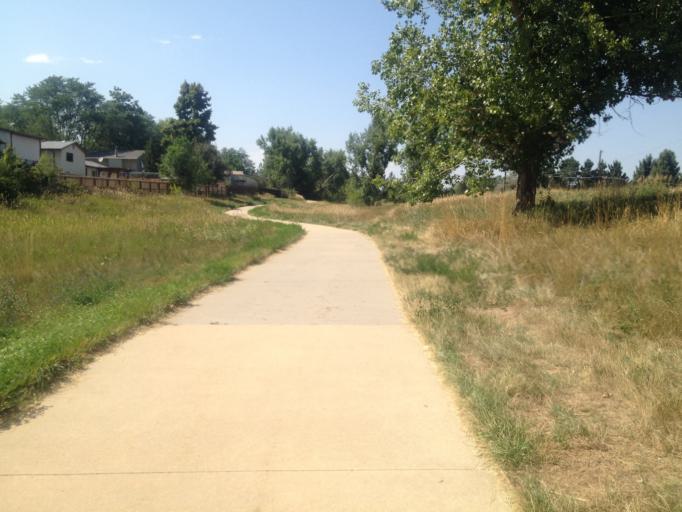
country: US
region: Colorado
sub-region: Boulder County
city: Louisville
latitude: 39.9960
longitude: -105.1391
